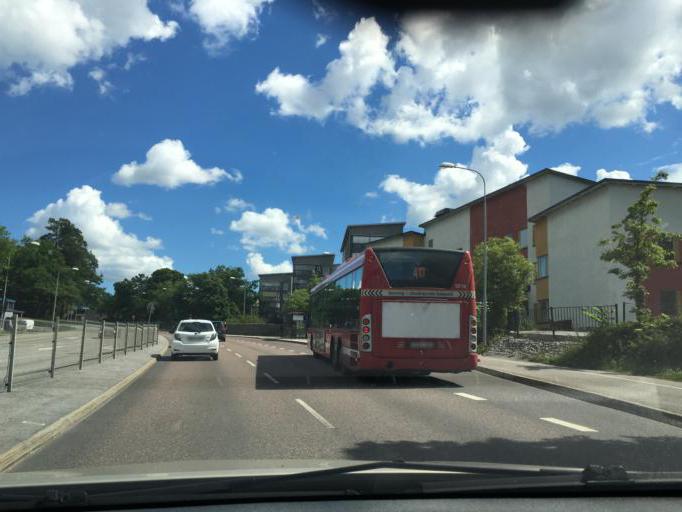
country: SE
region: Stockholm
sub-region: Nacka Kommun
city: Nacka
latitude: 59.3073
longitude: 18.1587
